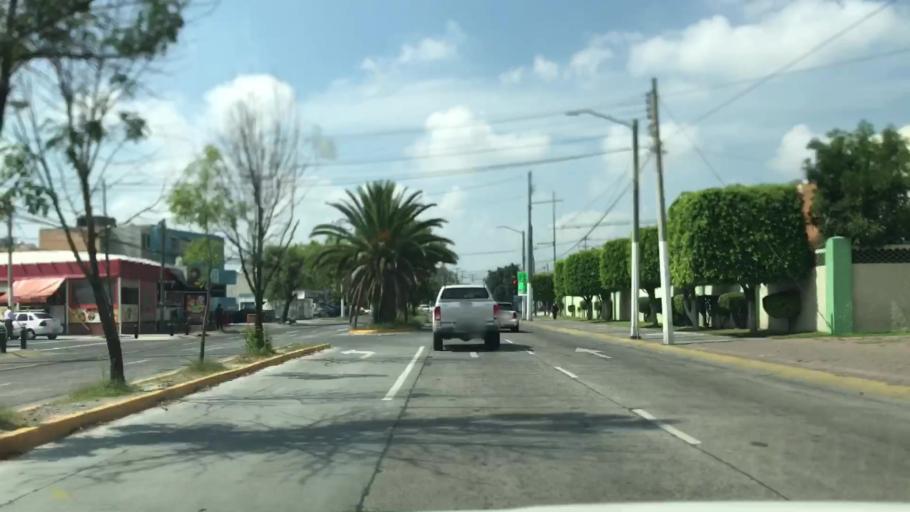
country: MX
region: Jalisco
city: Guadalajara
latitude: 20.6560
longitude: -103.4216
